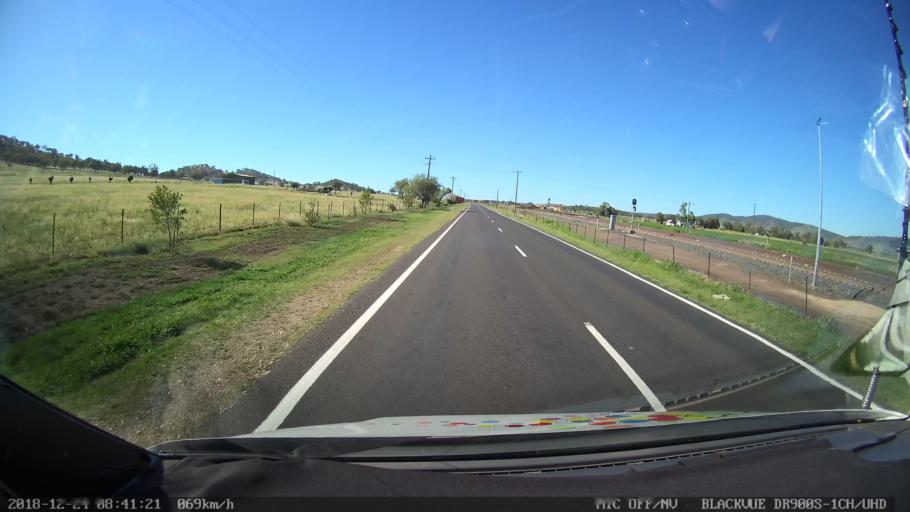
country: AU
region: New South Wales
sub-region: Liverpool Plains
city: Quirindi
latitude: -31.3623
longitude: 150.6451
